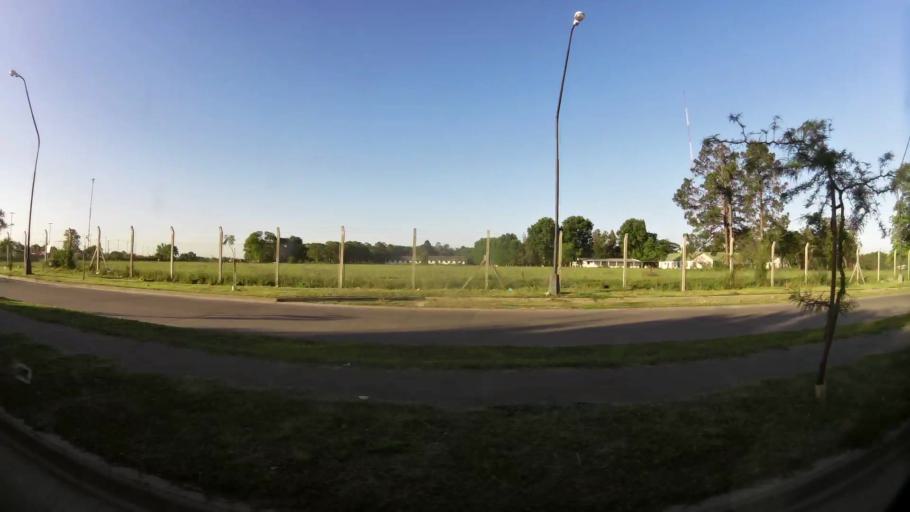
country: AR
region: Santa Fe
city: Santa Fe de la Vera Cruz
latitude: -31.5961
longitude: -60.6751
